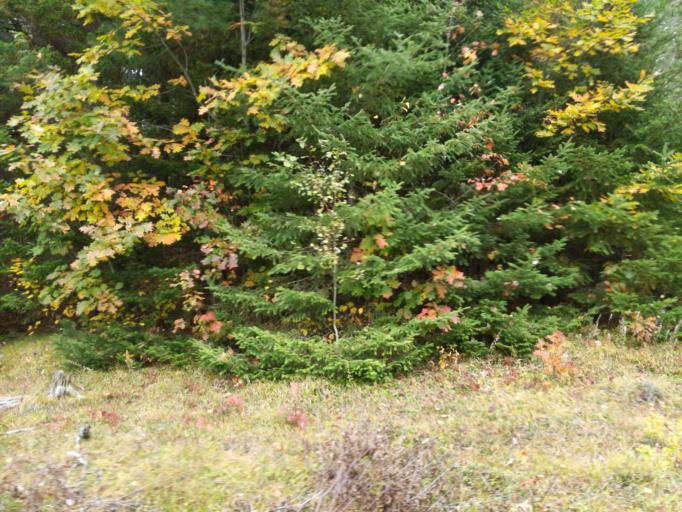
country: US
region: Maine
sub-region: Lincoln County
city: Wiscasset
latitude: 44.0763
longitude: -69.6222
